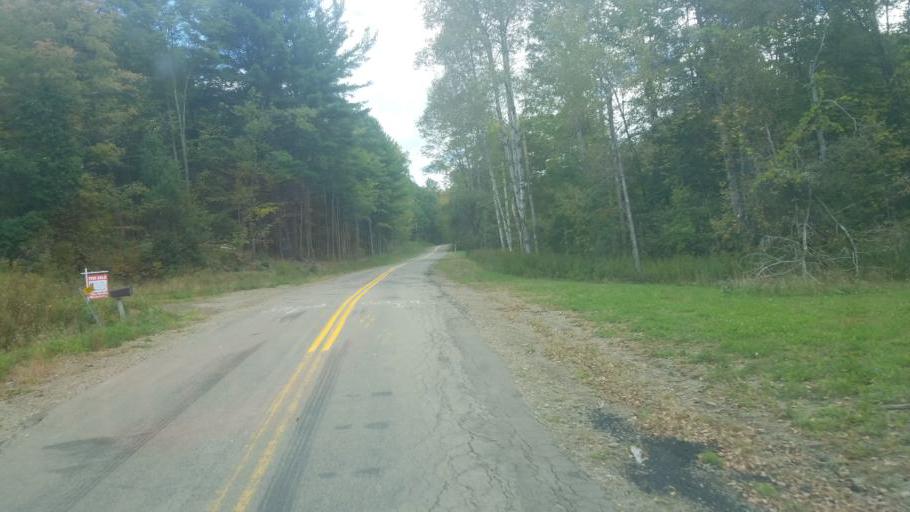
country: US
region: New York
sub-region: Allegany County
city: Cuba
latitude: 42.2201
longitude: -78.3607
